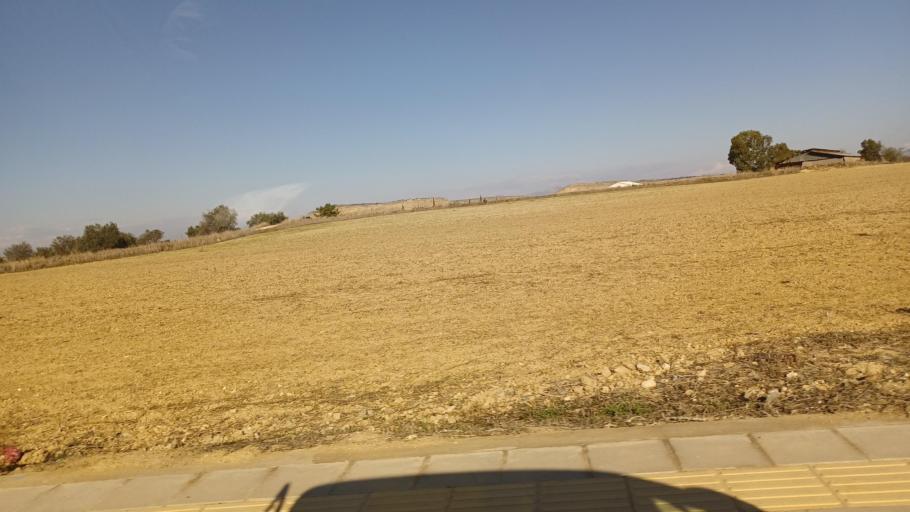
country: CY
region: Larnaka
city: Athienou
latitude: 35.0596
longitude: 33.5262
